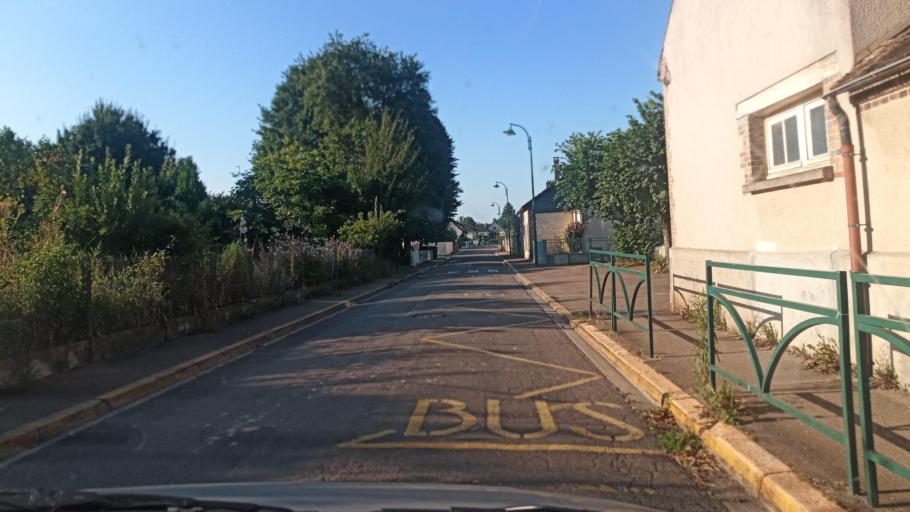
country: FR
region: Bourgogne
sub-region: Departement de l'Yonne
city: Saint-Valerien
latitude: 48.1787
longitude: 3.0938
